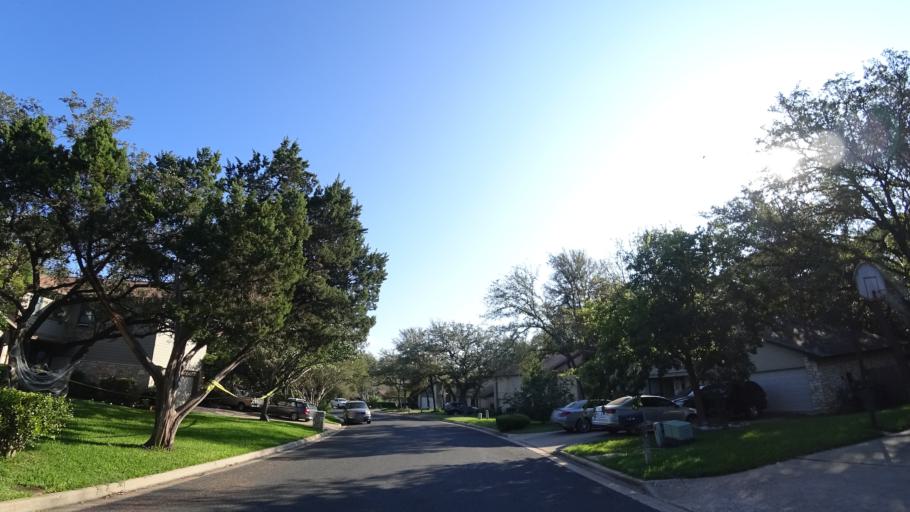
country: US
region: Texas
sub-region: Travis County
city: Rollingwood
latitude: 30.2649
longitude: -97.8057
